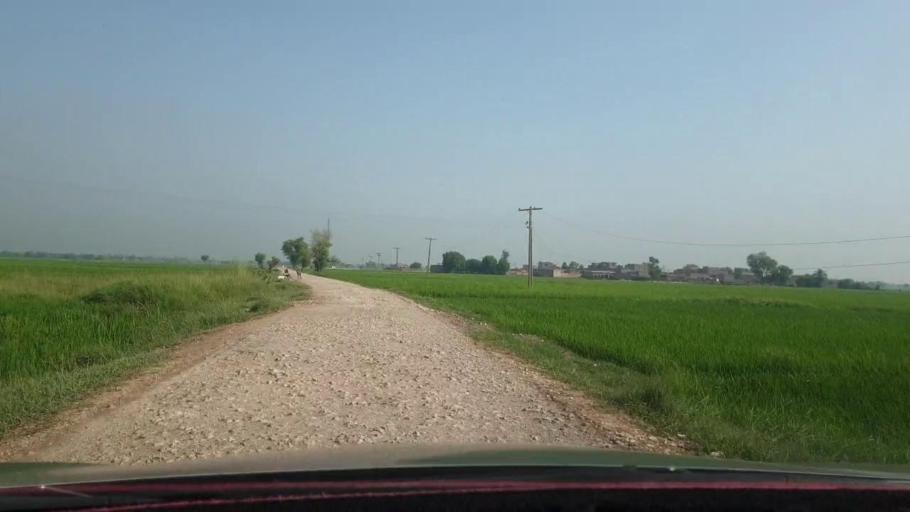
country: PK
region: Sindh
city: Nasirabad
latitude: 27.4806
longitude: 67.9257
